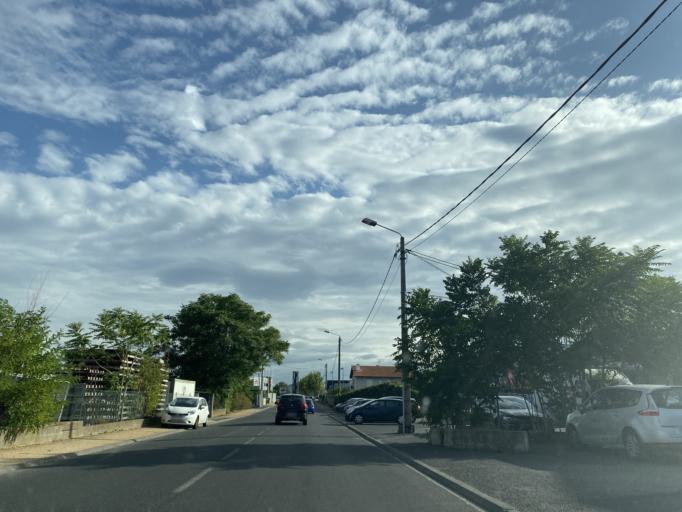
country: FR
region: Auvergne
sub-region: Departement du Puy-de-Dome
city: Perignat-les-Sarlieve
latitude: 45.7552
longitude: 3.1377
